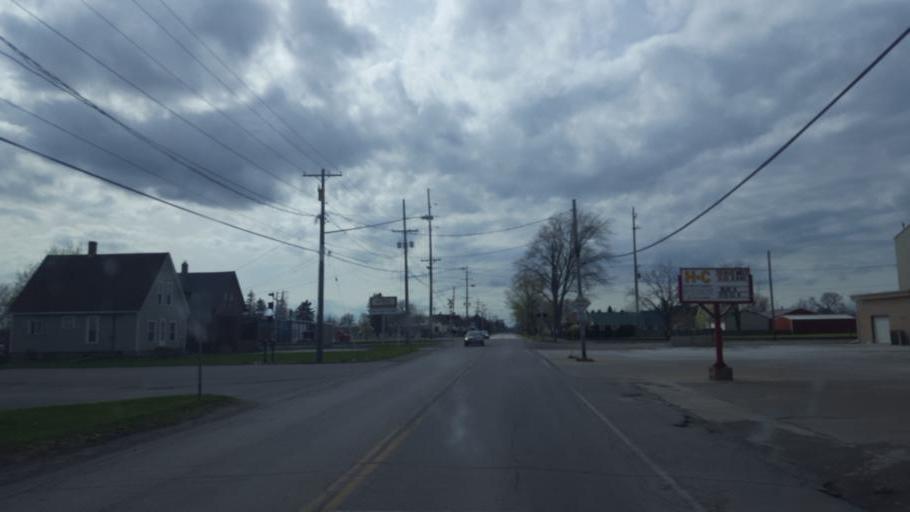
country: US
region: Ohio
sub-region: Erie County
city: Sandusky
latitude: 41.4406
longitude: -82.7393
